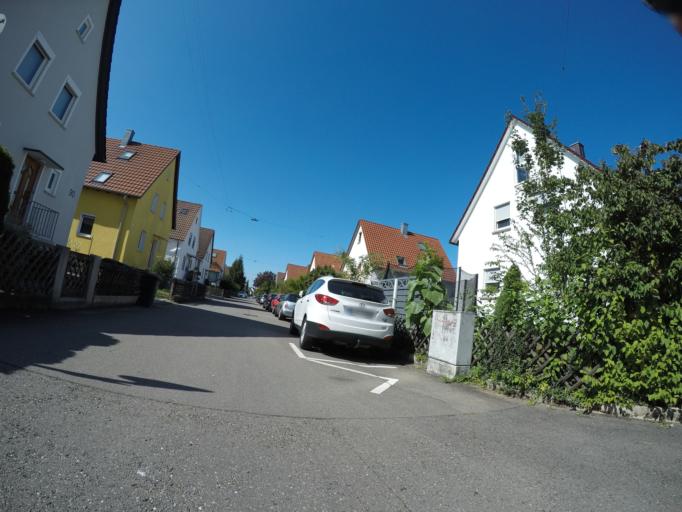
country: DE
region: Baden-Wuerttemberg
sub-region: Tuebingen Region
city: Reutlingen
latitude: 48.4962
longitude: 9.1870
